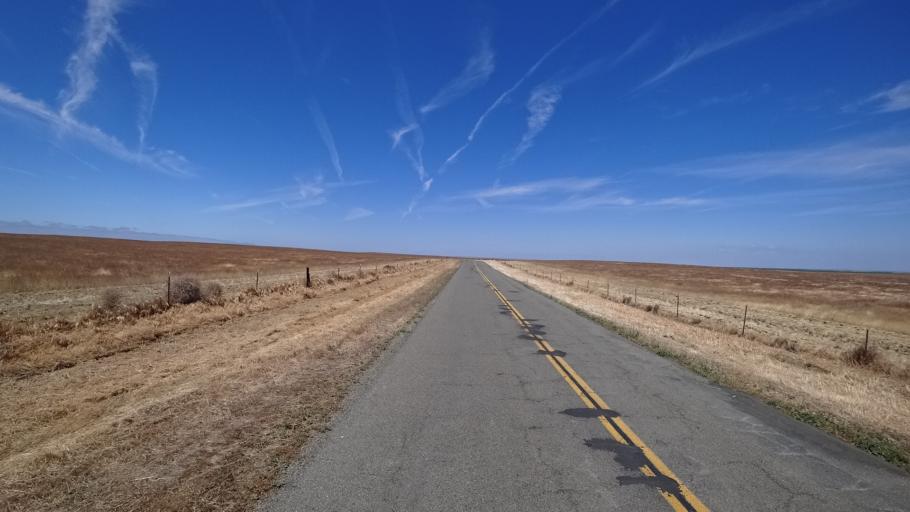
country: US
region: California
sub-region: Kings County
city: Kettleman City
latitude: 35.7910
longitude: -119.8902
